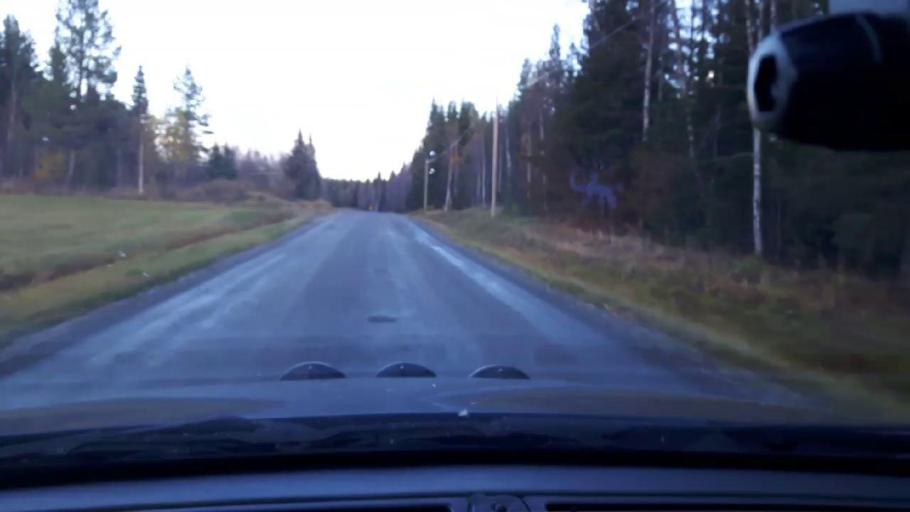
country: SE
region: Jaemtland
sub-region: Bergs Kommun
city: Hoverberg
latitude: 63.0655
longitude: 14.2621
